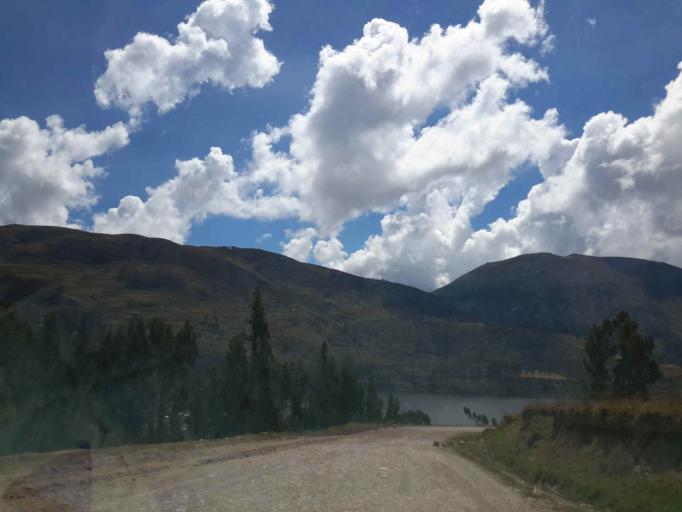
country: PE
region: Apurimac
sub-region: Provincia de Andahuaylas
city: Pacucha
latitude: -13.6184
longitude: -73.3338
